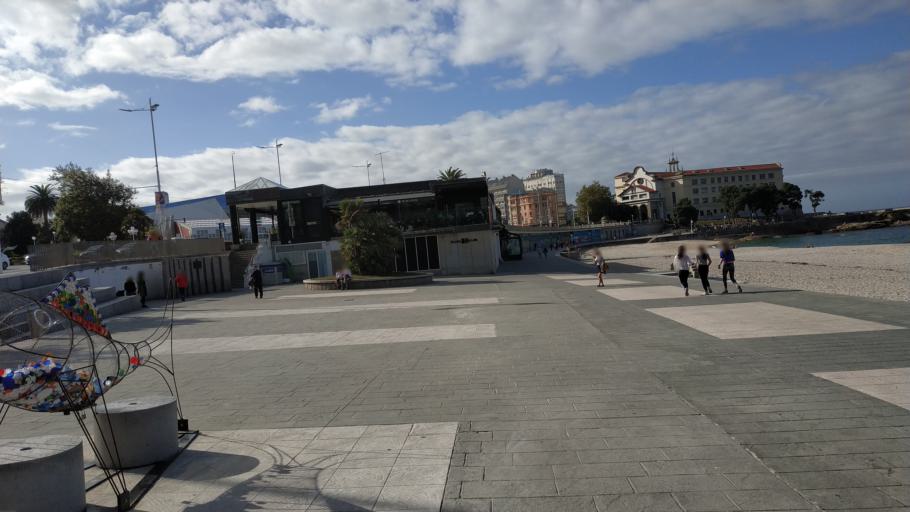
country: ES
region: Galicia
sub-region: Provincia da Coruna
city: A Coruna
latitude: 43.3682
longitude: -8.4127
